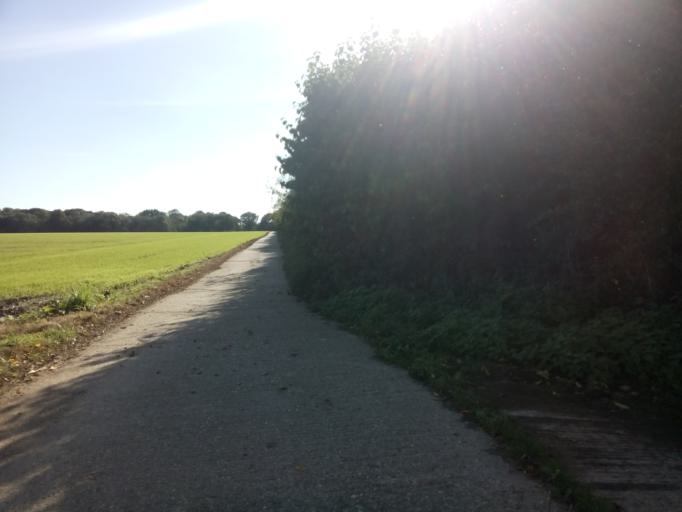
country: GB
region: England
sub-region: Suffolk
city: Ipswich
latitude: 52.0148
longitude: 1.1386
